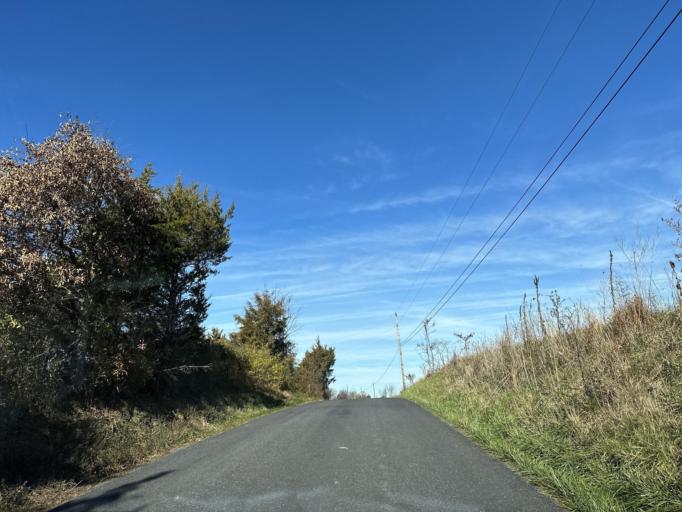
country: US
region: Virginia
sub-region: Augusta County
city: Weyers Cave
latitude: 38.2514
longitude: -78.9217
